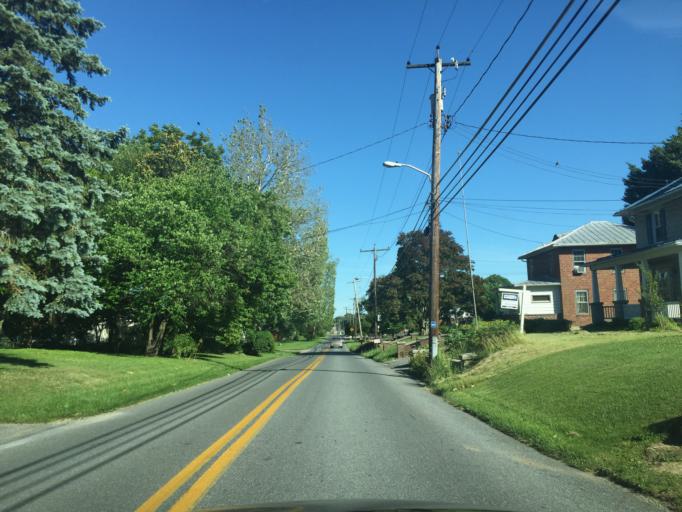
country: US
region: Maryland
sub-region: Carroll County
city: Hampstead
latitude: 39.5436
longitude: -76.8348
